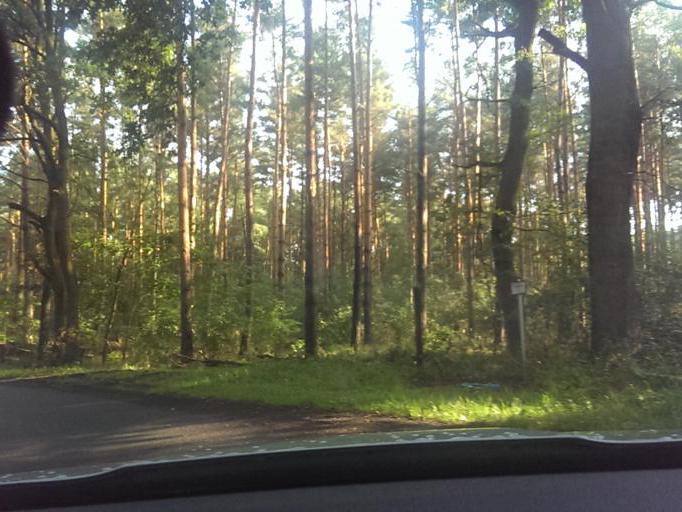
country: DE
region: Lower Saxony
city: Elze
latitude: 52.5638
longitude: 9.7962
